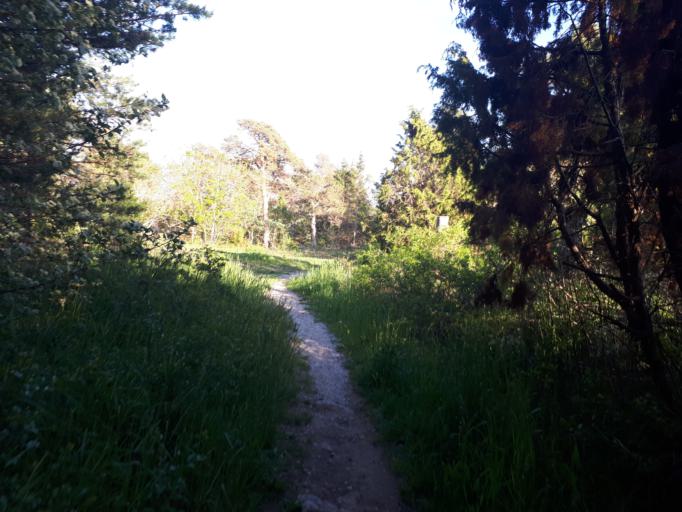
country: SE
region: Gotland
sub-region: Gotland
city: Visby
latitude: 57.6019
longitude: 18.3013
